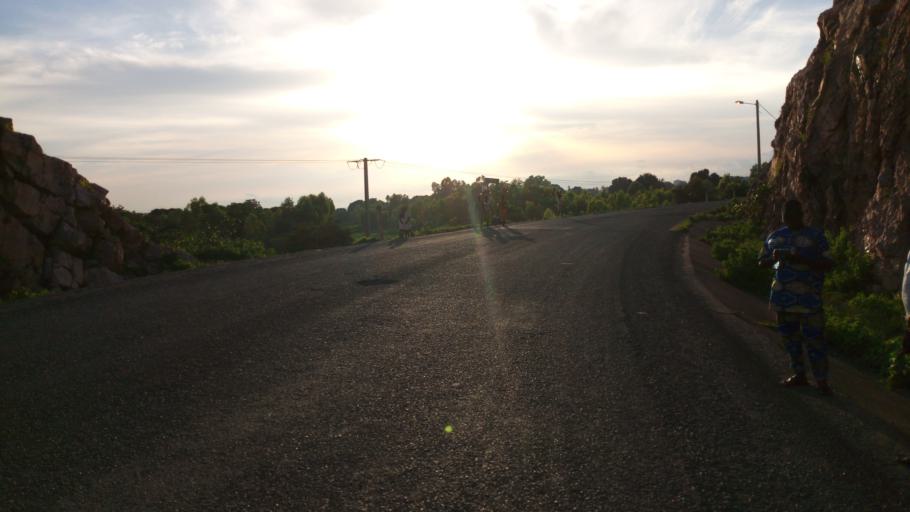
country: BJ
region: Atakora
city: Tanguieta
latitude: 10.6126
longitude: 1.2763
